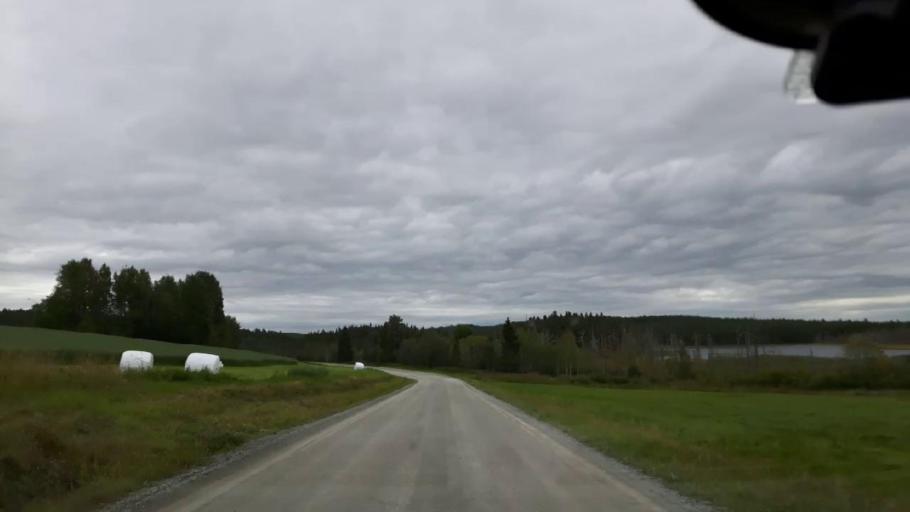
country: SE
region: Jaemtland
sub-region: OEstersunds Kommun
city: Brunflo
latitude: 63.0879
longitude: 15.1484
